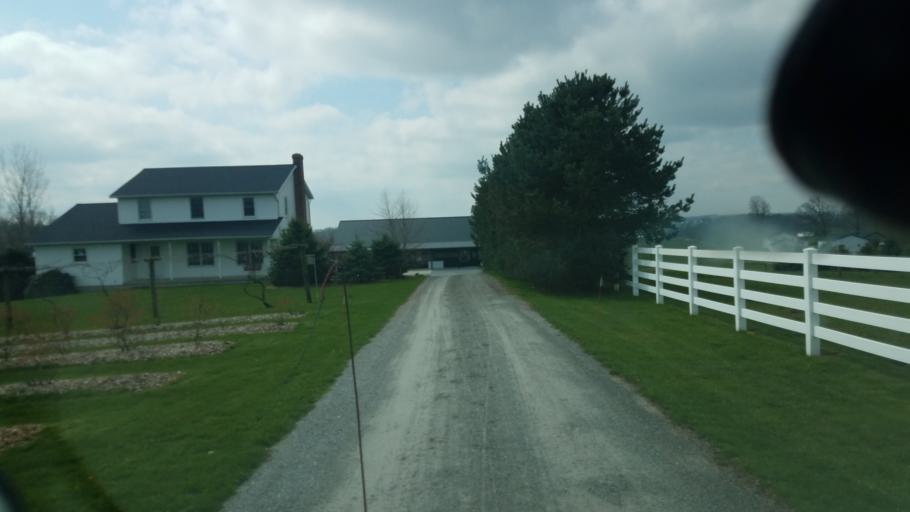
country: US
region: Ohio
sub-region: Holmes County
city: Millersburg
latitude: 40.6068
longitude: -81.7963
